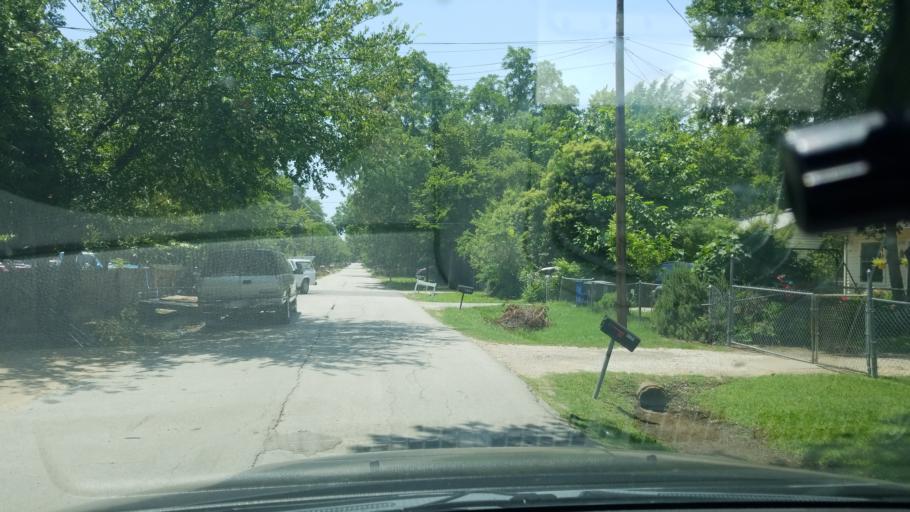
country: US
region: Texas
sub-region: Dallas County
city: Balch Springs
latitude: 32.7263
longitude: -96.6686
